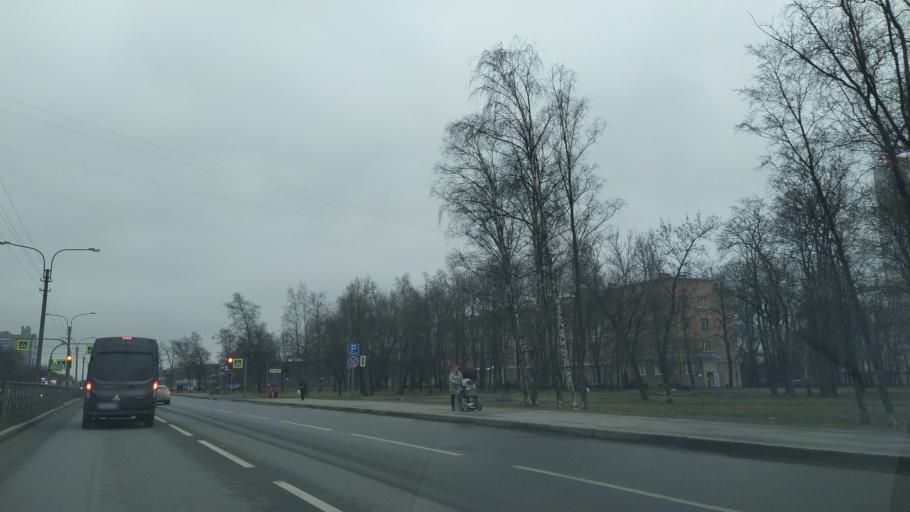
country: RU
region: St.-Petersburg
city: Kupchino
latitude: 59.8345
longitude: 30.3375
